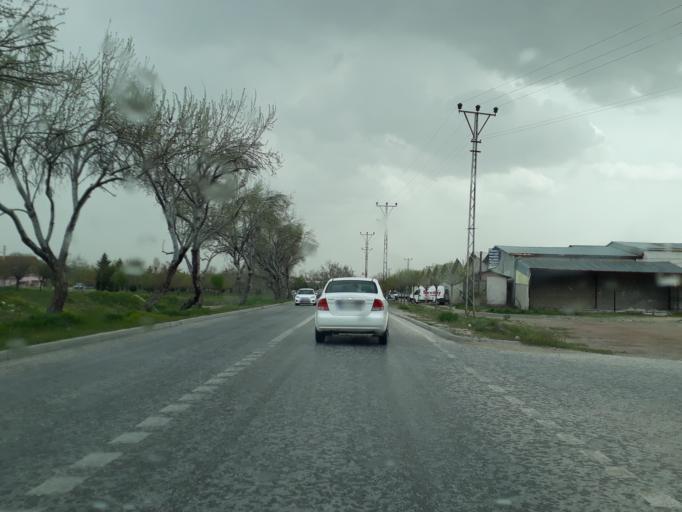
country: TR
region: Konya
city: Selcuklu
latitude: 37.9179
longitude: 32.4737
